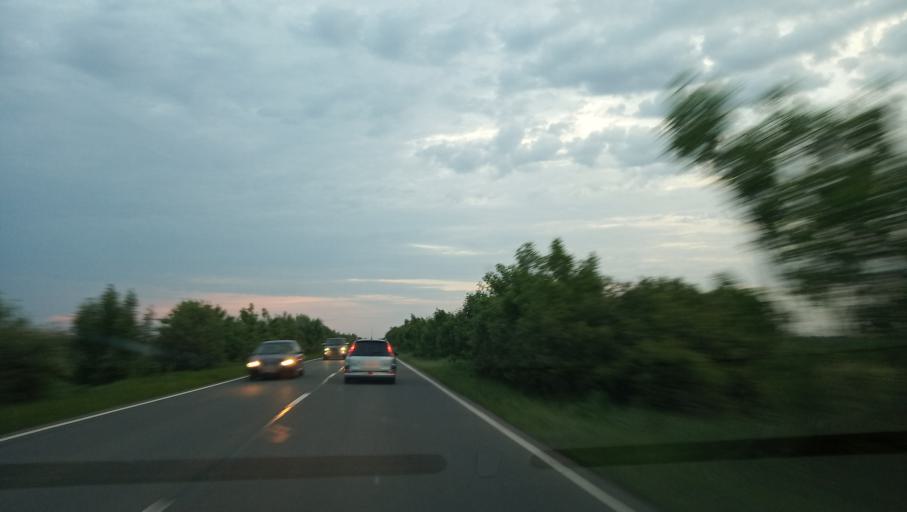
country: RO
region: Timis
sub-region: Comuna Padureni
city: Padureni
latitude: 45.6051
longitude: 21.1967
